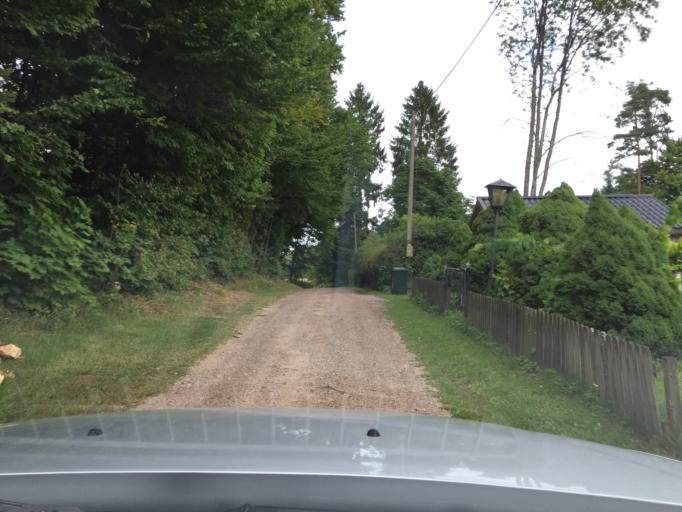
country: SE
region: Skane
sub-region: Hassleholms Kommun
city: Sosdala
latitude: 56.0063
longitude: 13.6366
